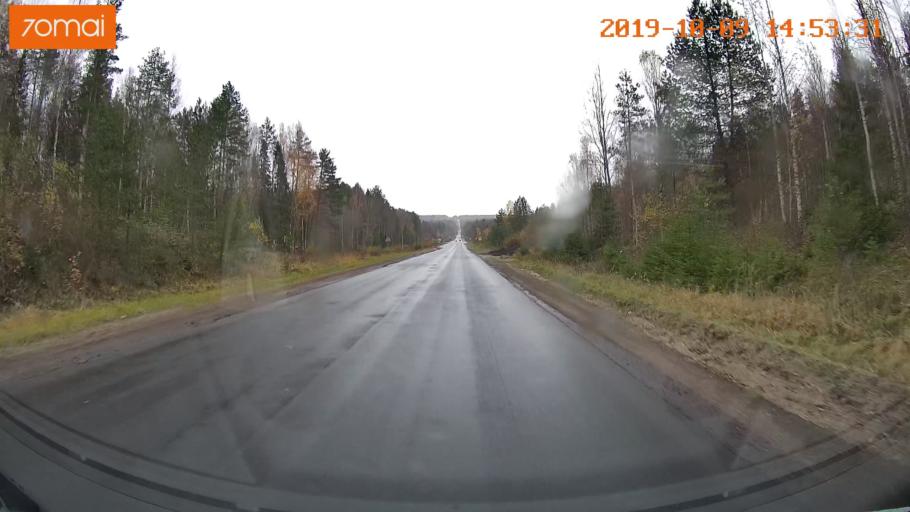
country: RU
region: Kostroma
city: Chistyye Bory
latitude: 58.3666
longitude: 41.6387
